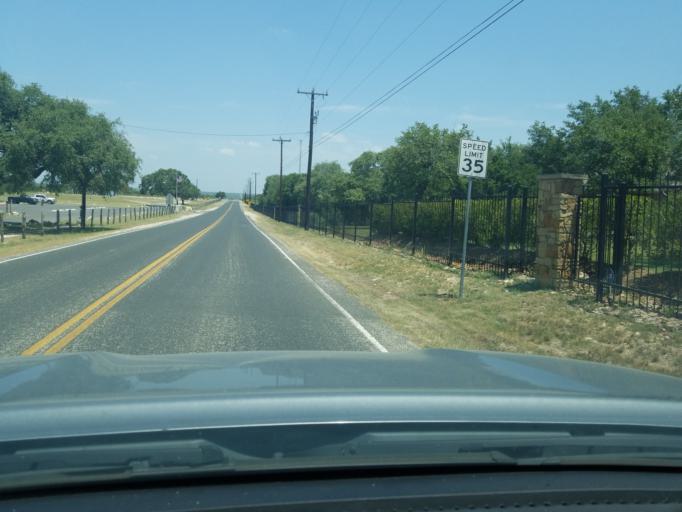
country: US
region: Texas
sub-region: Bexar County
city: Timberwood Park
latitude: 29.7092
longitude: -98.5129
